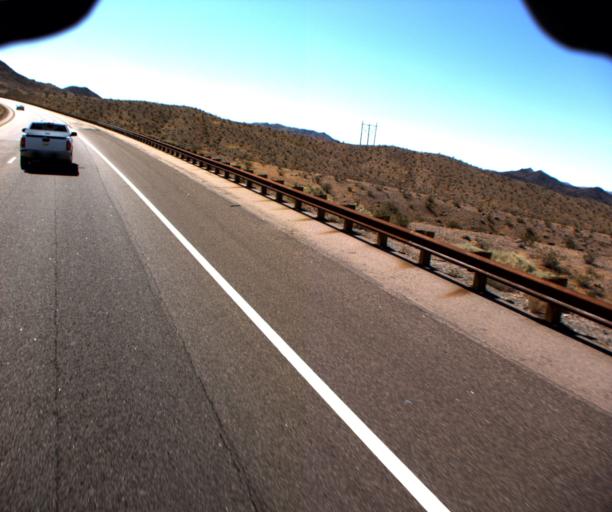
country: US
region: Nevada
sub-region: Clark County
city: Boulder City
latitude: 35.8612
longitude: -114.6011
